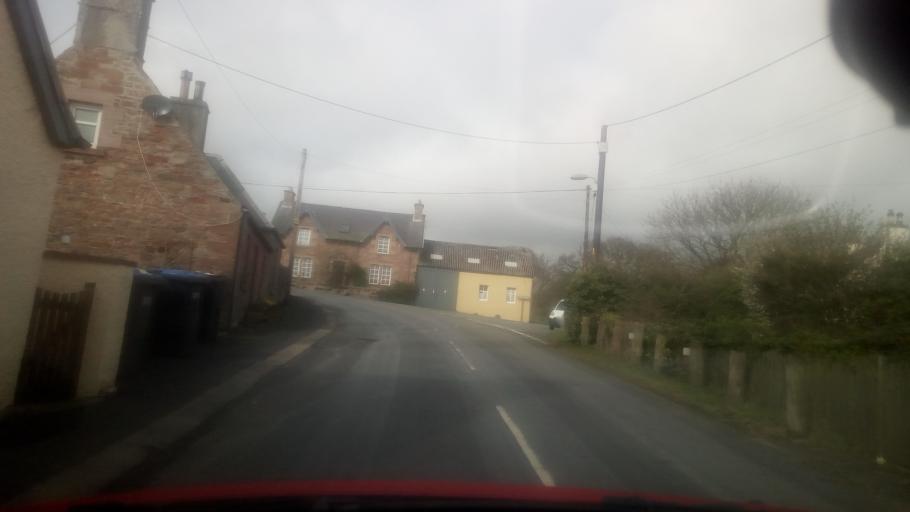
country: GB
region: Scotland
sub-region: The Scottish Borders
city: Saint Boswells
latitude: 55.5849
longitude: -2.6158
